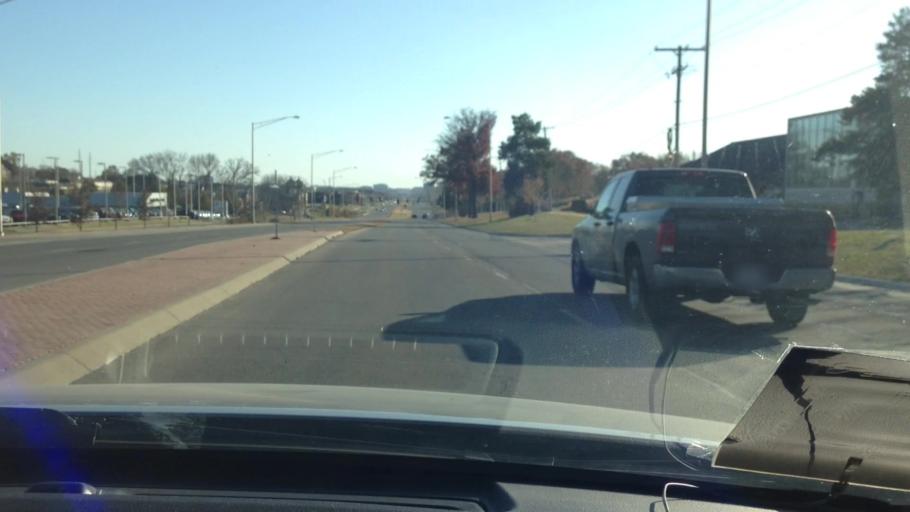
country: US
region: Kansas
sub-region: Johnson County
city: Overland Park
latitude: 38.9705
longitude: -94.6677
